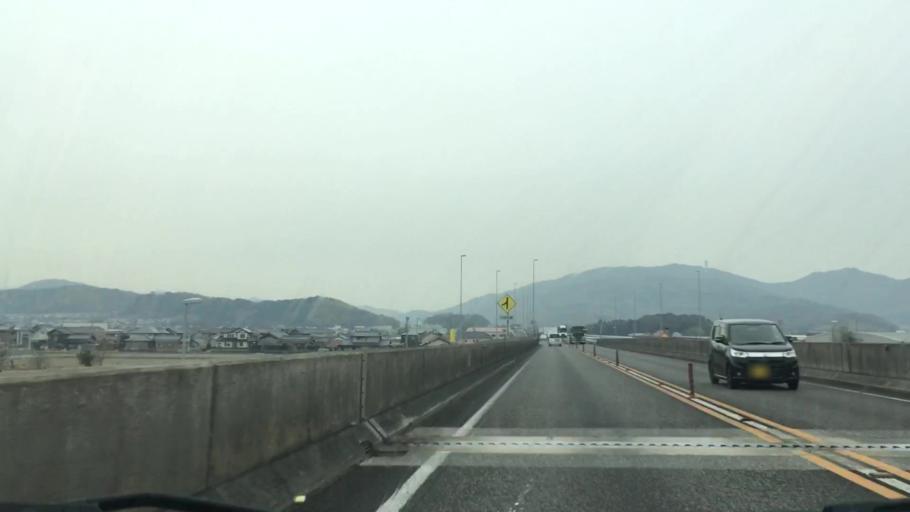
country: JP
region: Aichi
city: Nishio
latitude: 34.8670
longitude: 137.0907
